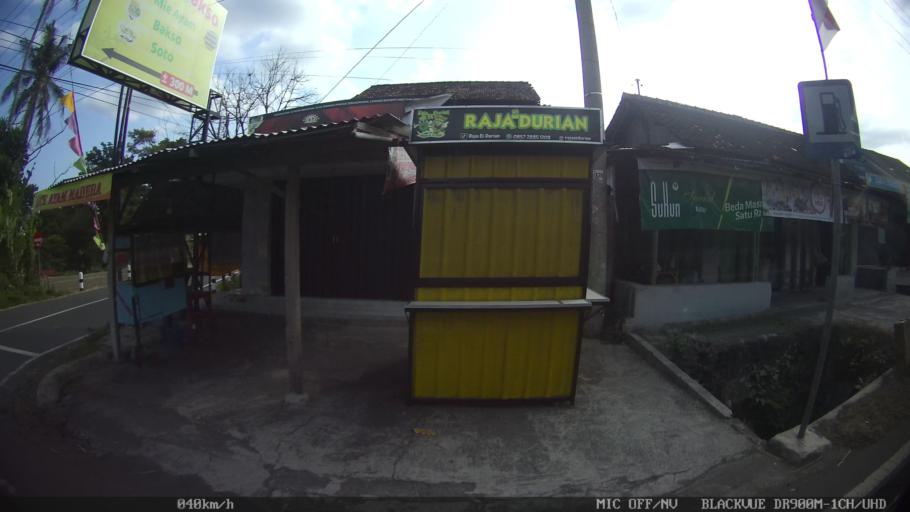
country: ID
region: Central Java
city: Candi Prambanan
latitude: -7.6969
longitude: 110.4644
